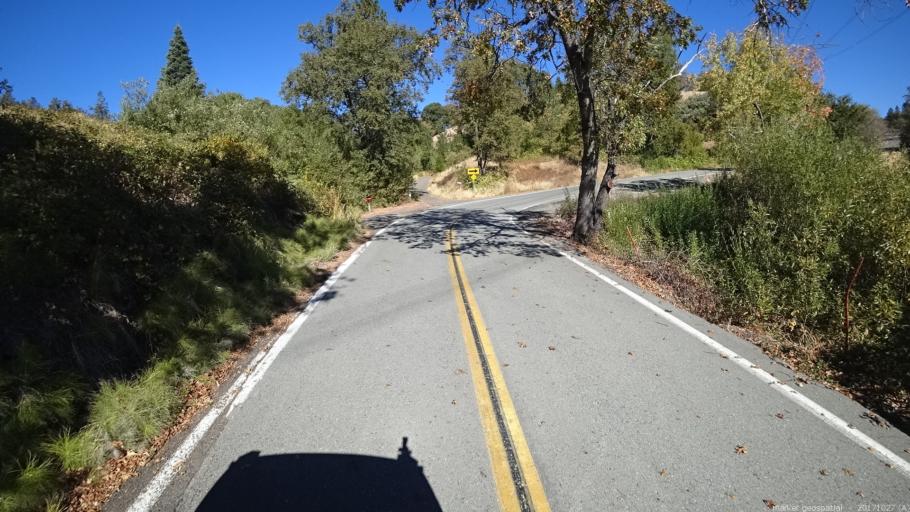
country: US
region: California
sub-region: Shasta County
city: Bella Vista
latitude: 40.7522
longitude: -121.9957
